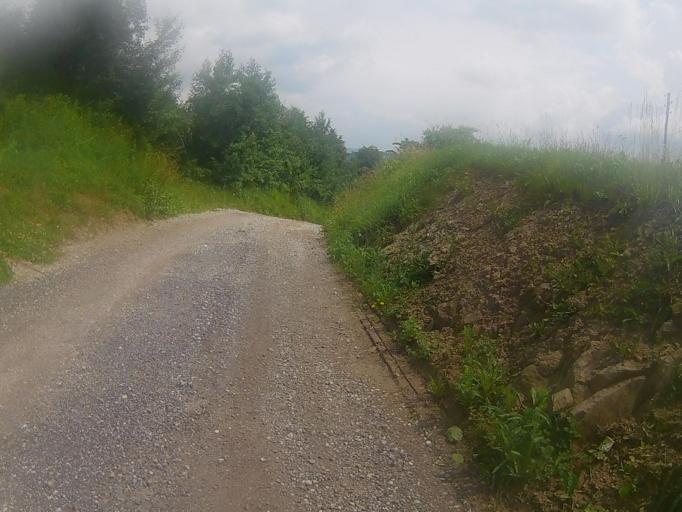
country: SI
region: Kungota
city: Zgornja Kungota
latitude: 46.6340
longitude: 15.6005
